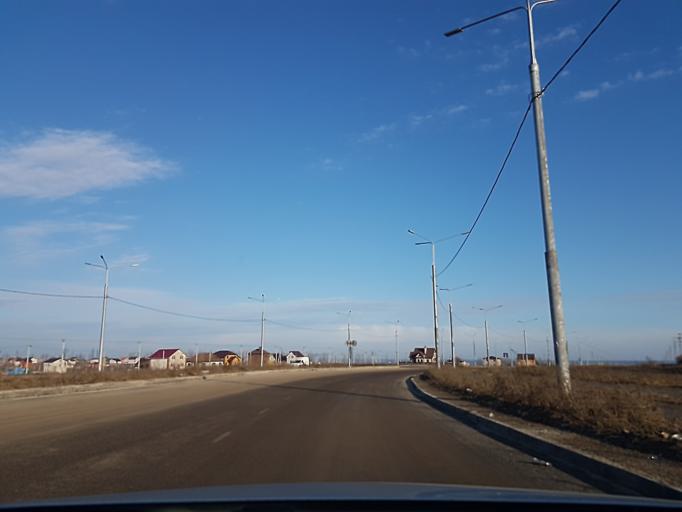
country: RU
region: Tambov
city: Tambov
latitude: 52.7819
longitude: 41.4105
